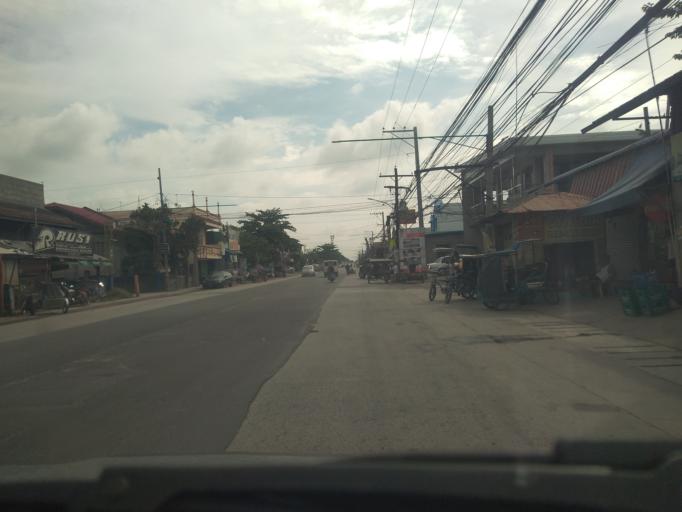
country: PH
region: Central Luzon
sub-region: Province of Pampanga
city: Pau
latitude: 15.0071
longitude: 120.7138
